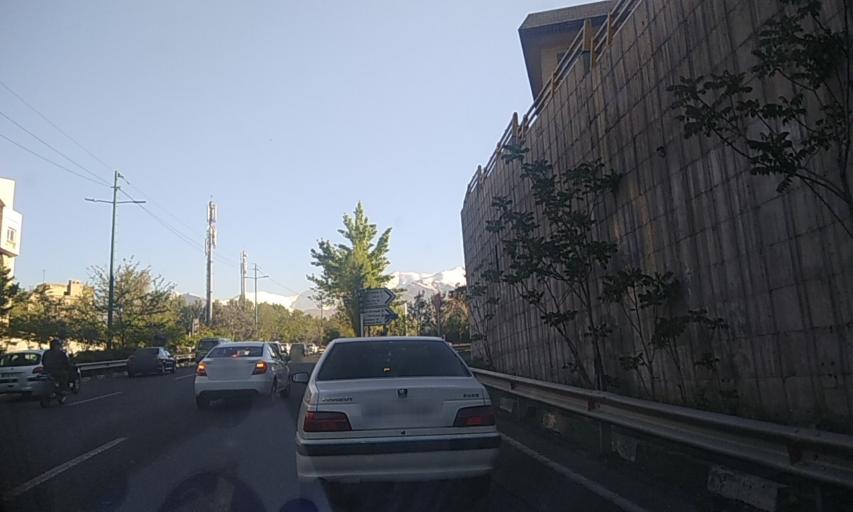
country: IR
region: Tehran
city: Tajrish
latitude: 35.7645
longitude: 51.4027
